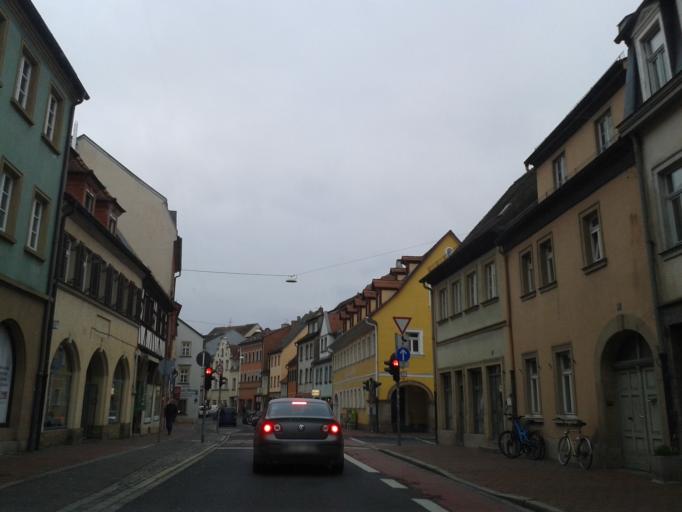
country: DE
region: Bavaria
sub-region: Upper Franconia
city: Bamberg
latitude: 49.8987
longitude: 10.8892
